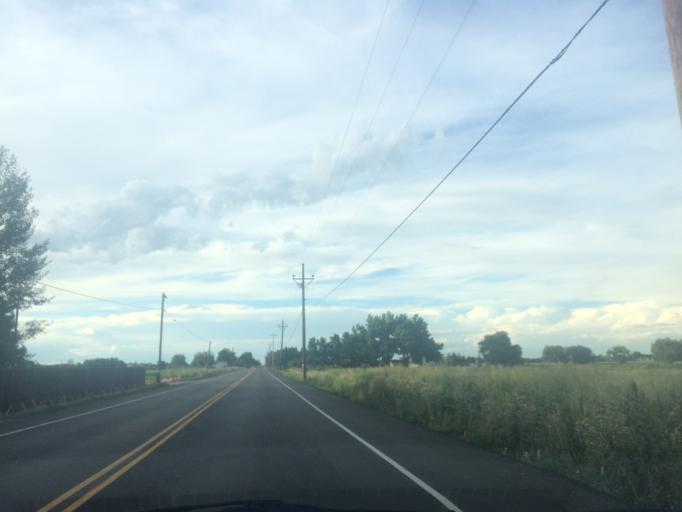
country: US
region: Colorado
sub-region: Boulder County
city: Niwot
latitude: 40.1193
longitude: -105.1310
